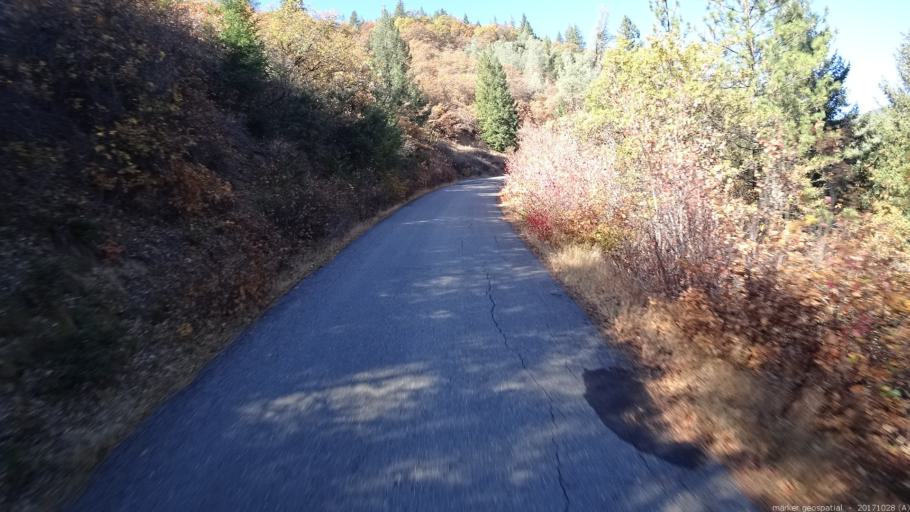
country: US
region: California
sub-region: Trinity County
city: Lewiston
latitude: 40.8067
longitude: -122.6120
